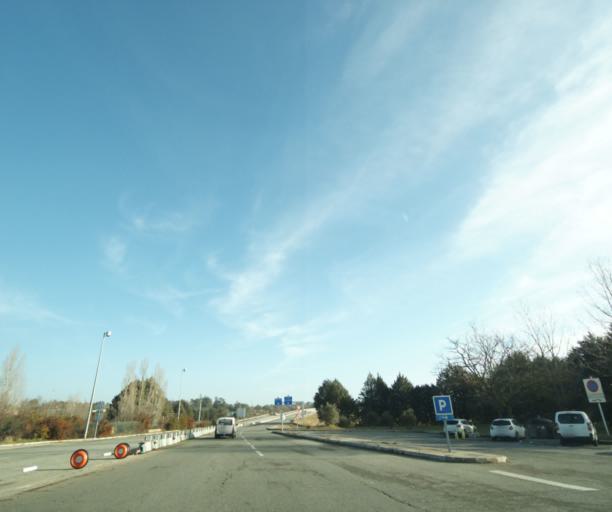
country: FR
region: Provence-Alpes-Cote d'Azur
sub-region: Departement du Var
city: Saint-Maximin-la-Sainte-Baume
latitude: 43.4495
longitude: 5.8775
